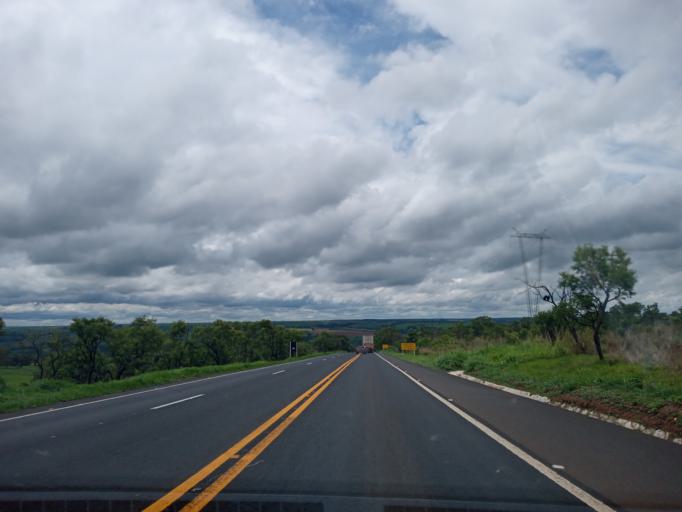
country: BR
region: Minas Gerais
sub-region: Uberaba
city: Uberaba
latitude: -19.2890
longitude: -47.6108
